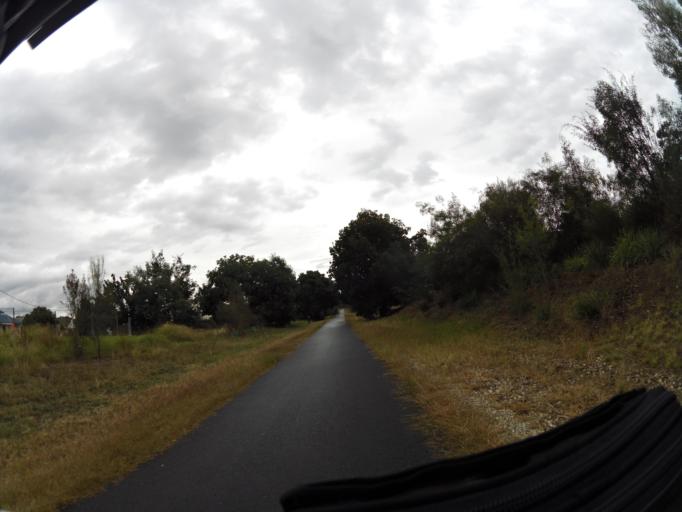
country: AU
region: Victoria
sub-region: Wodonga
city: Wodonga
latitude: -36.1273
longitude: 146.8951
